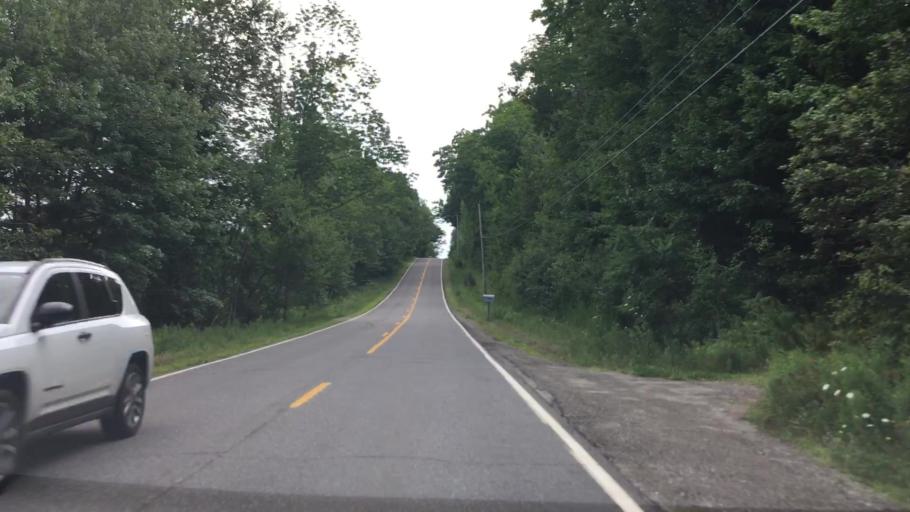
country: US
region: Maine
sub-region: Waldo County
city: Belfast
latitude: 44.3619
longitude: -69.0448
